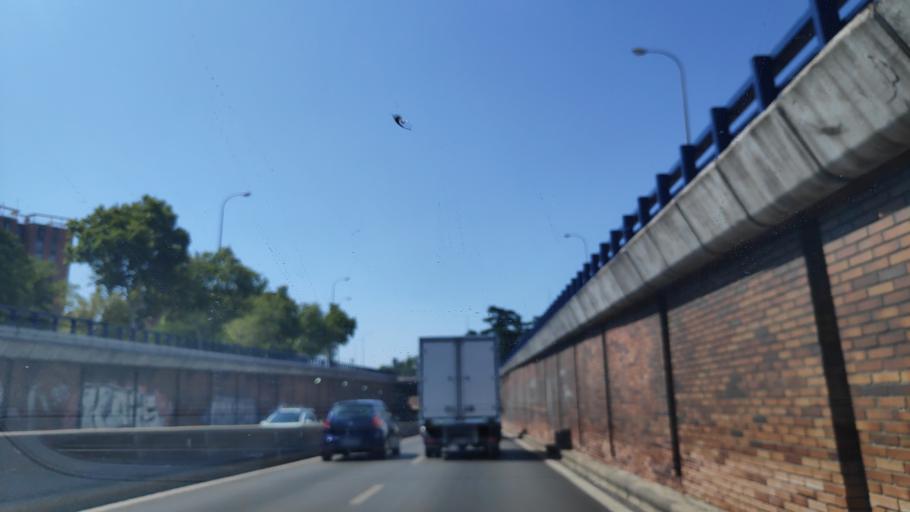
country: ES
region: Madrid
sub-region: Provincia de Madrid
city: Carabanchel
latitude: 40.3866
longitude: -3.7162
